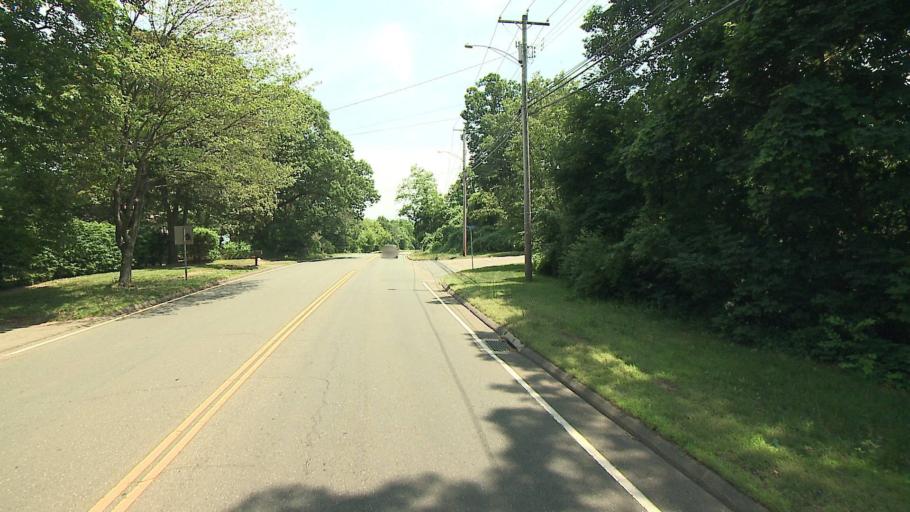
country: US
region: Connecticut
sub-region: New Haven County
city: Hamden
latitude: 41.3819
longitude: -72.8886
